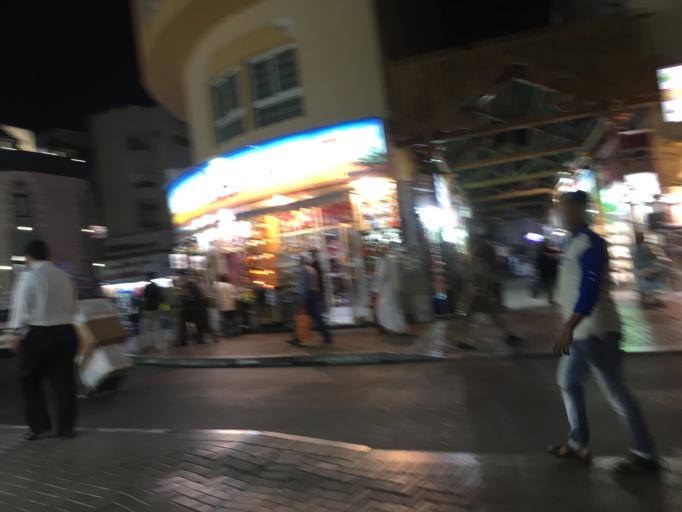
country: AE
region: Ash Shariqah
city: Sharjah
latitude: 25.2682
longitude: 55.2975
